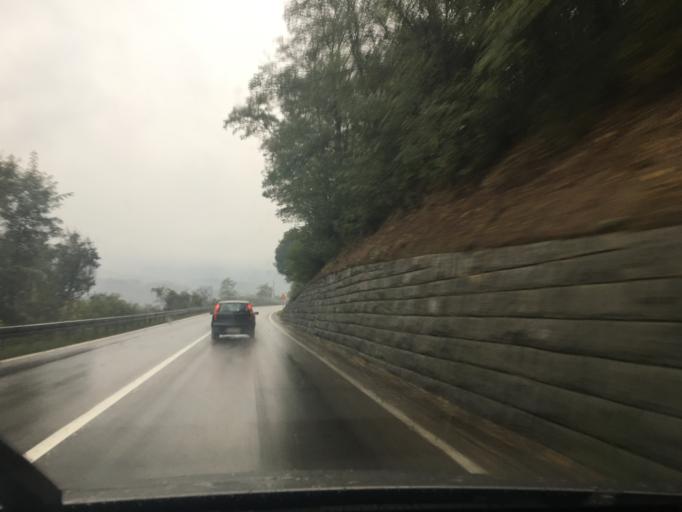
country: RS
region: Central Serbia
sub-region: Pcinjski Okrug
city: Vladicin Han
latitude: 42.7891
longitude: 22.0924
